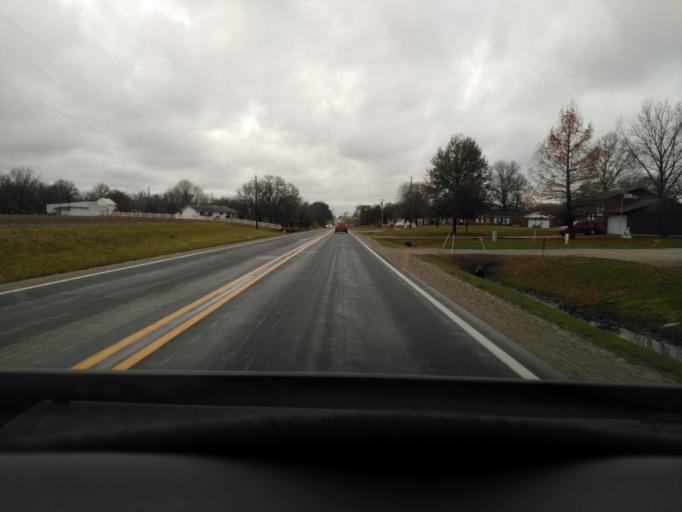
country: US
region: Illinois
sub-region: Effingham County
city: Altamont
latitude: 39.0378
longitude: -88.7482
